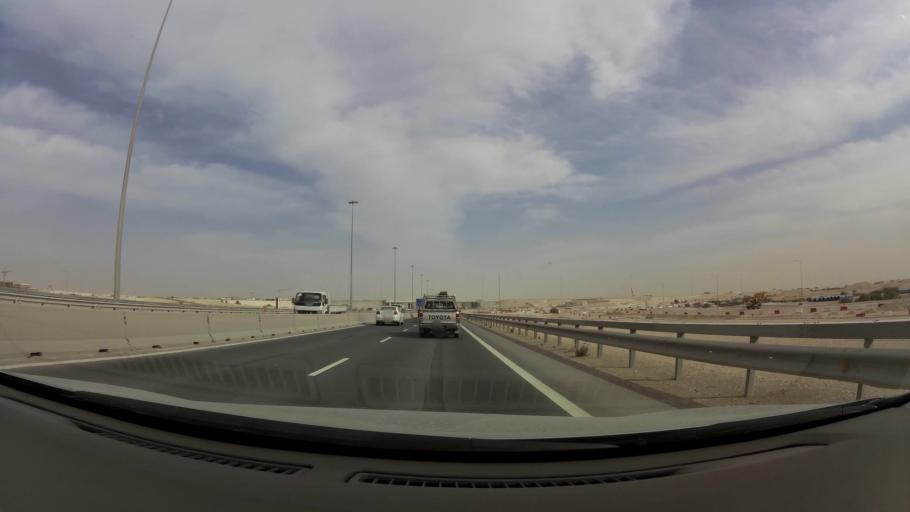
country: QA
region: Baladiyat ar Rayyan
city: Ar Rayyan
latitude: 25.3340
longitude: 51.3285
